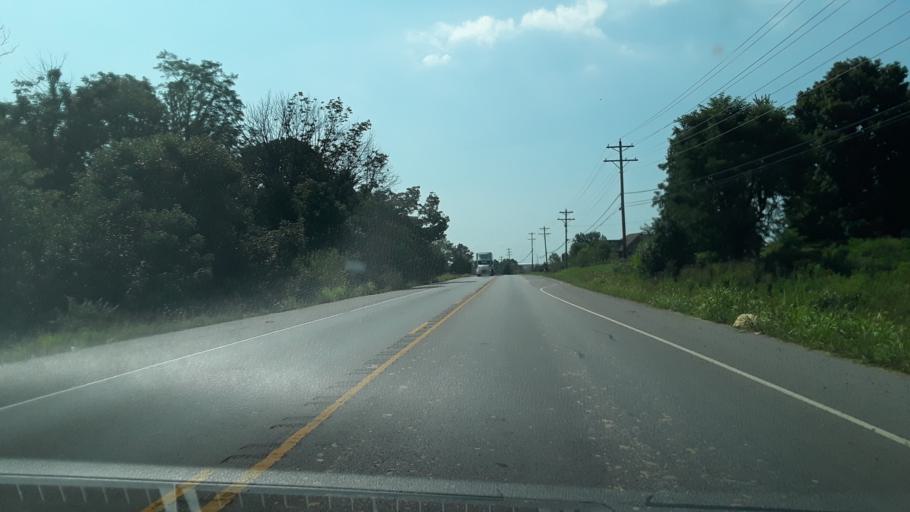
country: US
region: Indiana
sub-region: Clark County
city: Sellersburg
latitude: 38.3983
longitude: -85.7821
